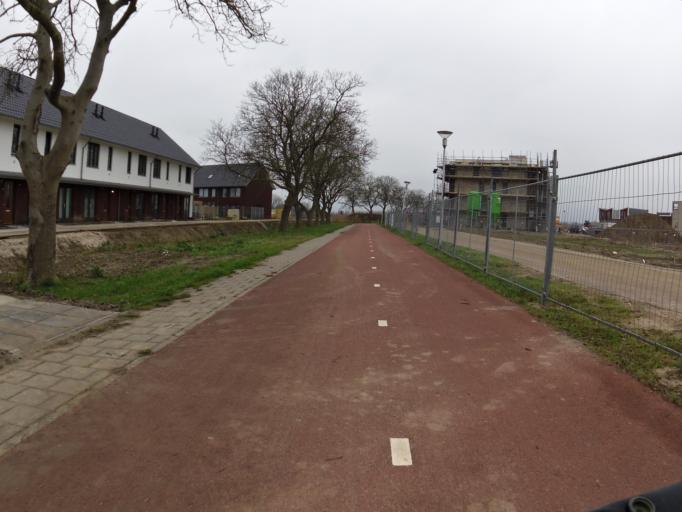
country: NL
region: Gelderland
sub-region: Gemeente Nijmegen
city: Nijmegen
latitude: 51.8728
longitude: 5.8638
